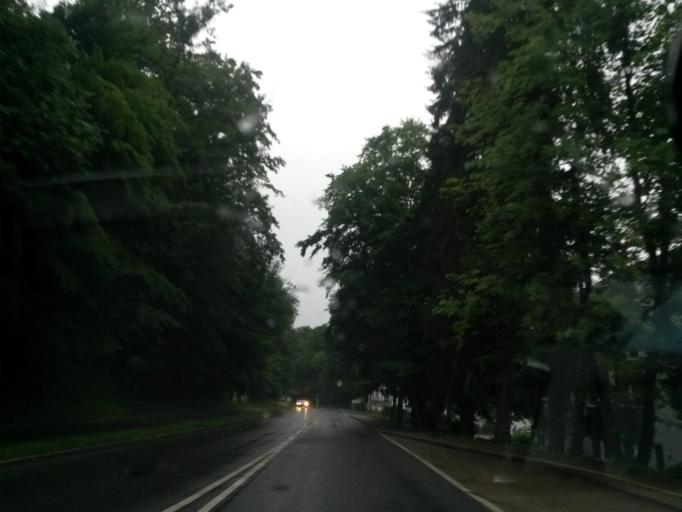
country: DE
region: North Rhine-Westphalia
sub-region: Regierungsbezirk Koln
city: Engelskirchen
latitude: 50.9898
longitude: 7.4572
